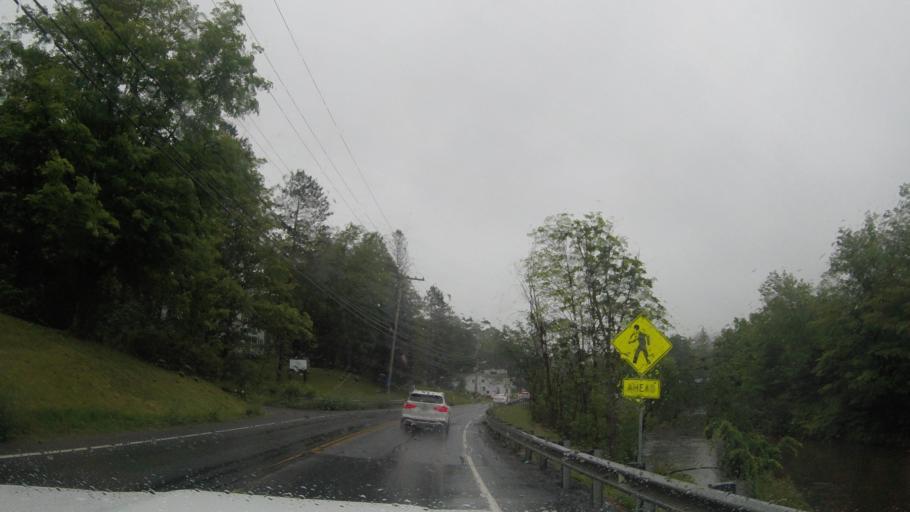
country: US
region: Vermont
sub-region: Windham County
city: Dover
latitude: 42.8706
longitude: -72.8753
